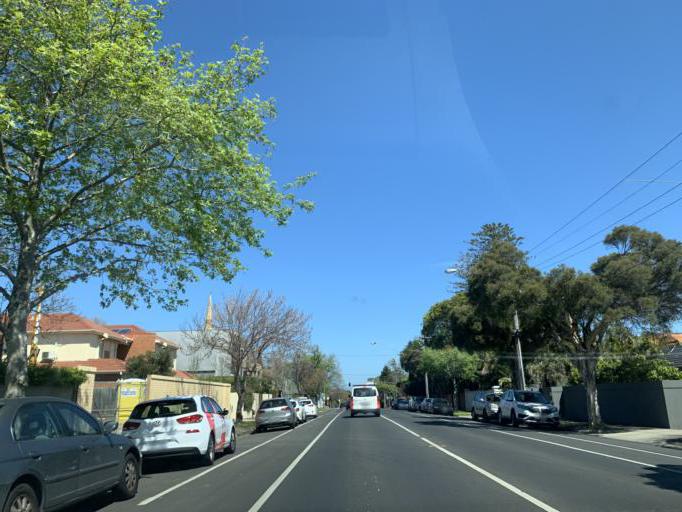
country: AU
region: Victoria
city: Ripponlea
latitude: -37.8967
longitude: 144.9946
